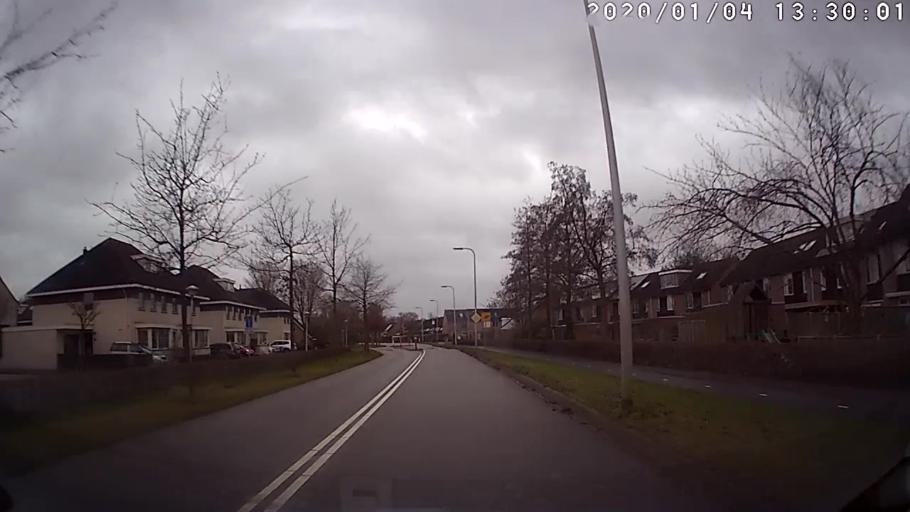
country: NL
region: Overijssel
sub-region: Gemeente Zwolle
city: Zwolle
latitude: 52.4781
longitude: 6.1161
